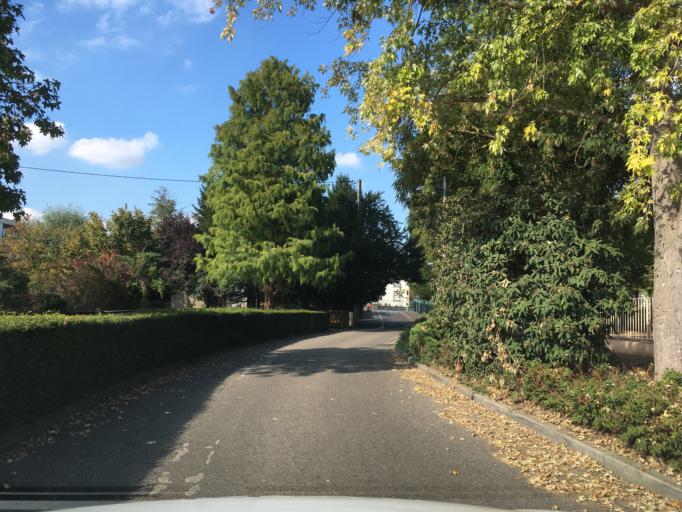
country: FR
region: Alsace
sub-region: Departement du Haut-Rhin
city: Colmar
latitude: 48.0684
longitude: 7.3588
